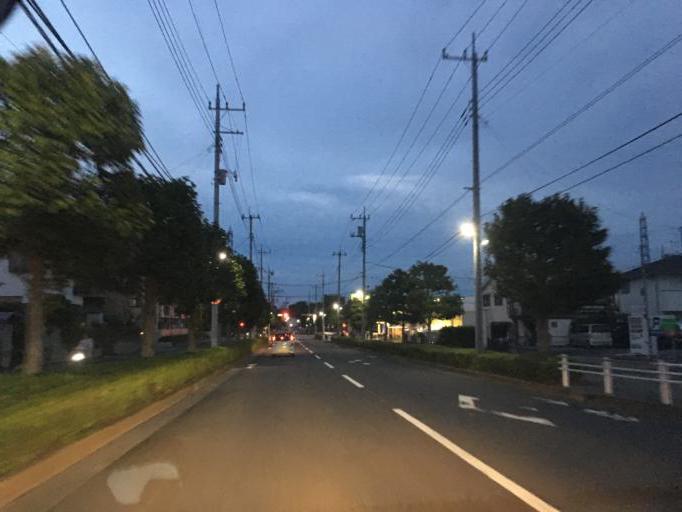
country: JP
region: Tokyo
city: Higashimurayama-shi
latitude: 35.7334
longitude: 139.4528
